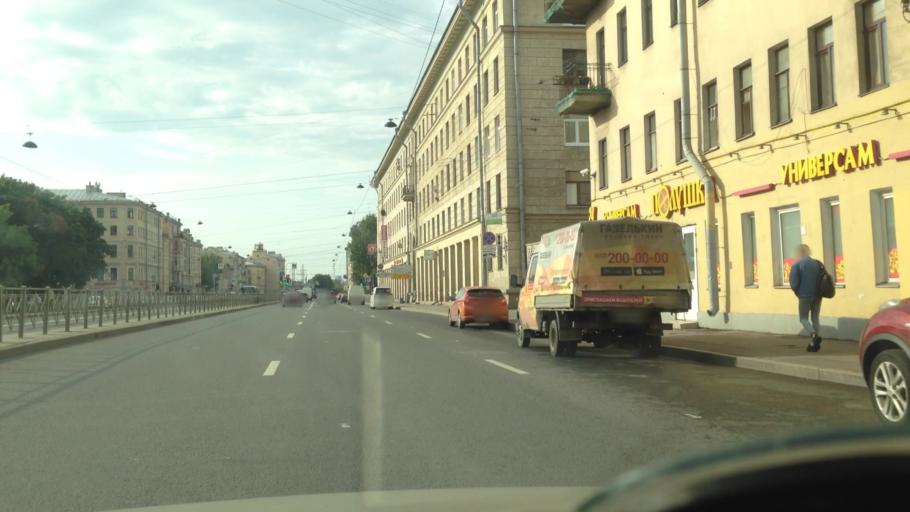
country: RU
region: St.-Petersburg
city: Centralniy
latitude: 59.9112
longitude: 30.3479
